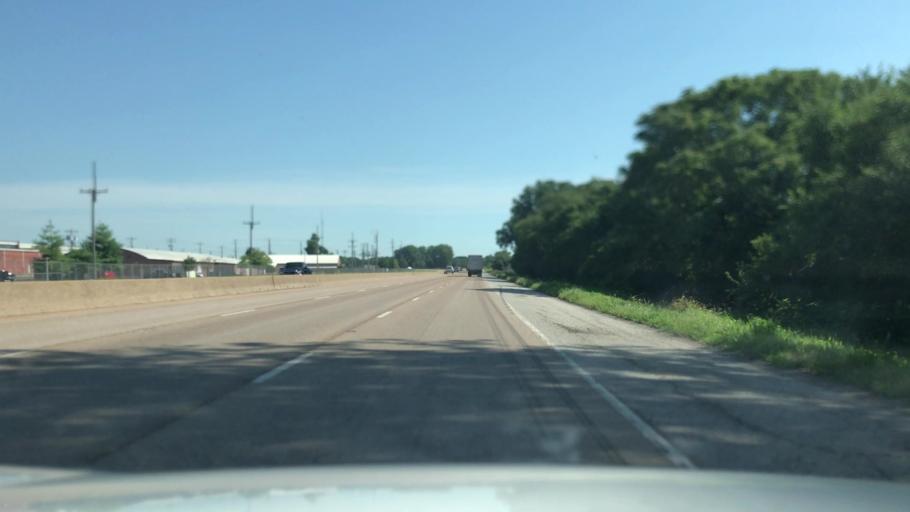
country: US
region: Illinois
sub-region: Madison County
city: Madison
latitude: 38.6877
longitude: -90.1711
